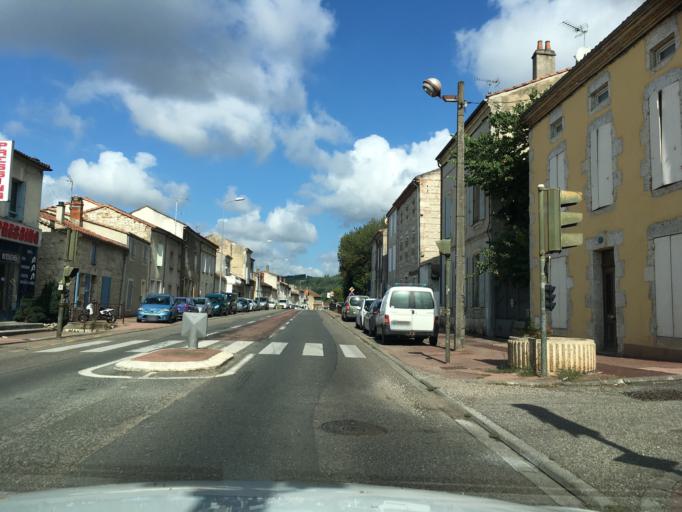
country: FR
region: Aquitaine
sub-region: Departement du Lot-et-Garonne
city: Le Passage
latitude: 44.2106
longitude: 0.6096
